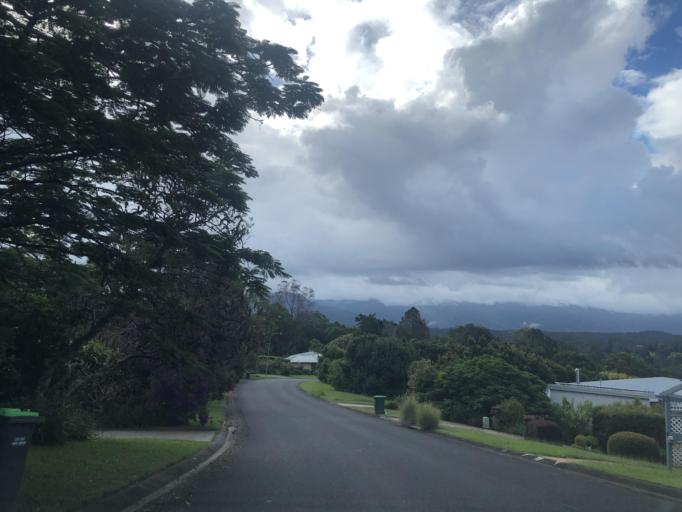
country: AU
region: New South Wales
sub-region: Bellingen
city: Bellingen
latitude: -30.4605
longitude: 152.9021
